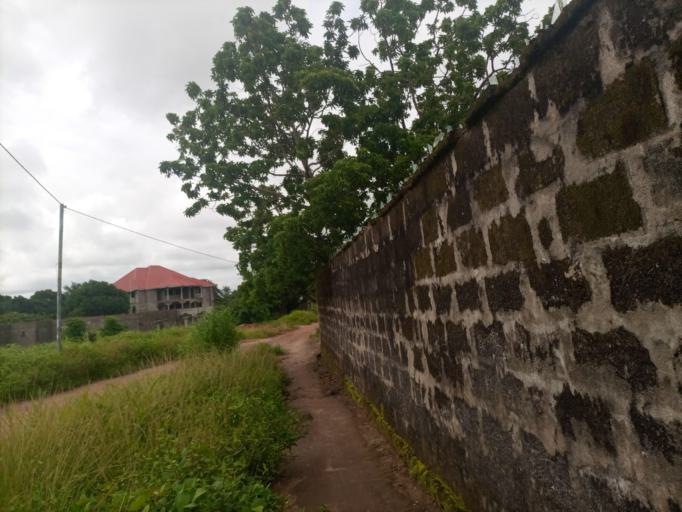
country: SL
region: Northern Province
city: Masoyila
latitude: 8.5958
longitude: -13.1763
